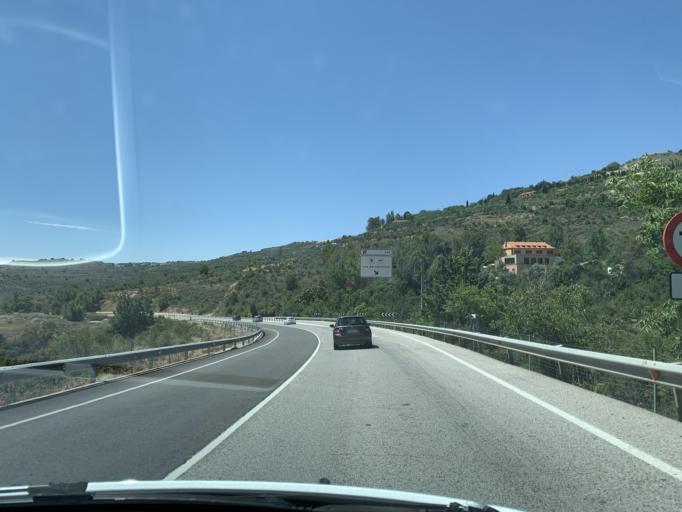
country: ES
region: Castille-La Mancha
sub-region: Provincia de Guadalajara
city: Horche
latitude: 40.5727
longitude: -3.0533
